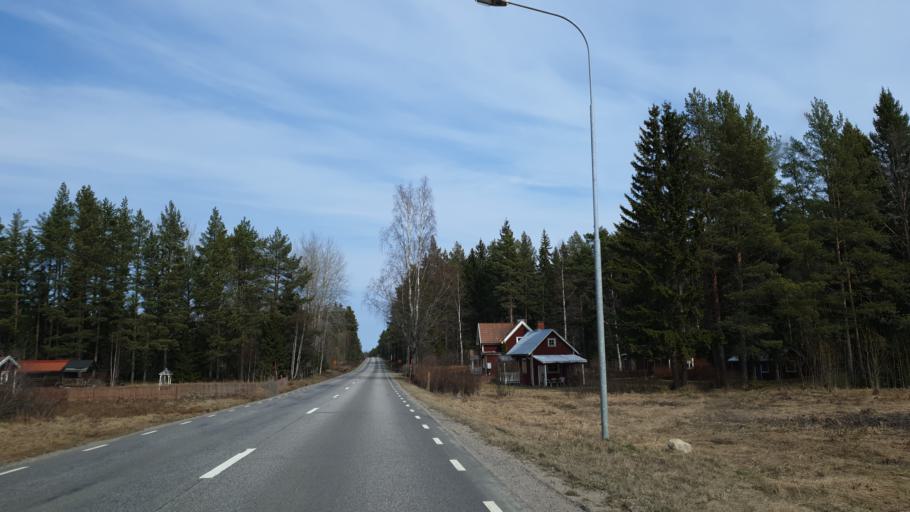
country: SE
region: Gaevleborg
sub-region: Gavle Kommun
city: Norrsundet
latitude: 61.0050
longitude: 17.1277
